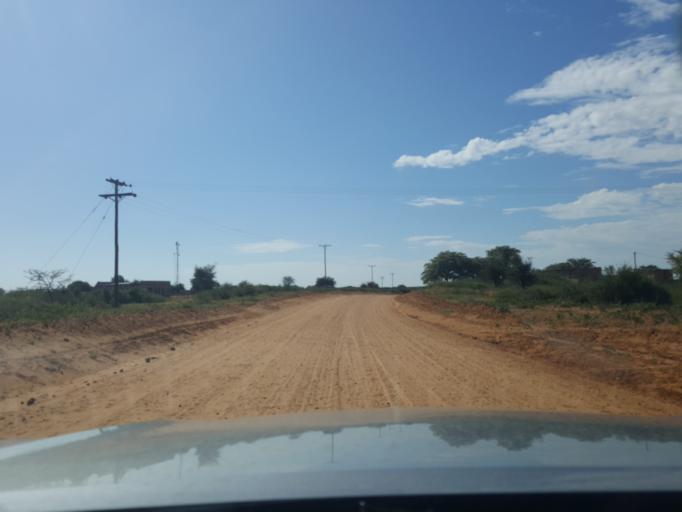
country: BW
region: Kweneng
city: Khudumelapye
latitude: -23.7014
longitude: 24.7215
